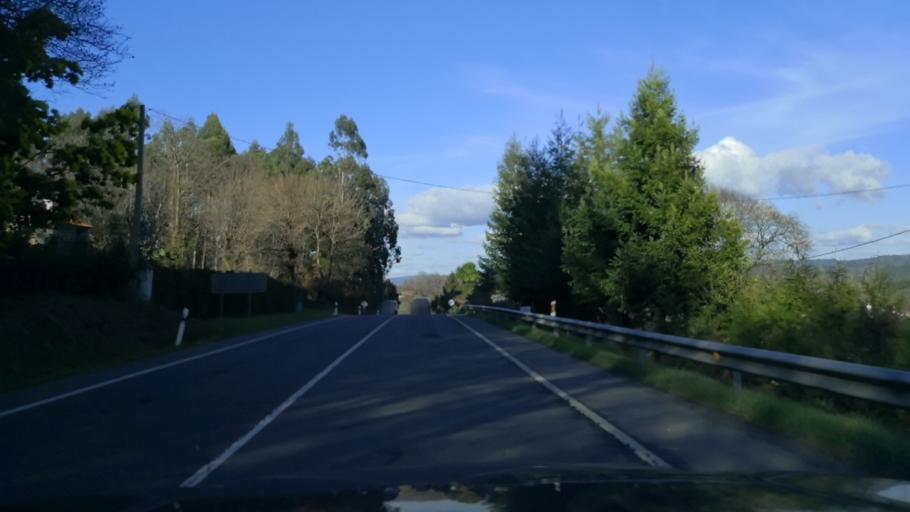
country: ES
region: Galicia
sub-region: Provincia de Pontevedra
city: Silleda
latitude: 42.7104
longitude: -8.2944
